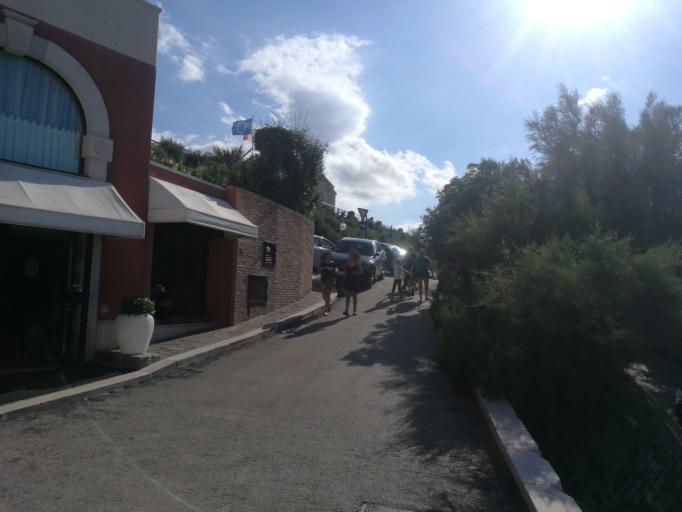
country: IT
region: Molise
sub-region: Provincia di Campobasso
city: Termoli
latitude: 42.0042
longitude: 14.9958
